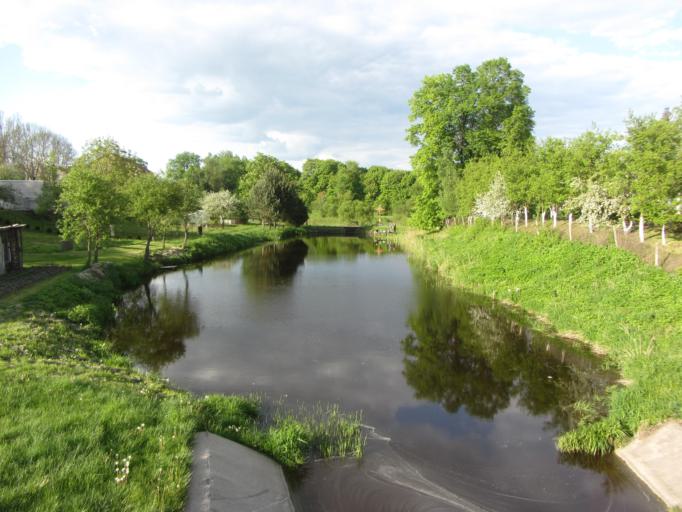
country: LT
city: Sirvintos
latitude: 55.0465
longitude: 24.9507
